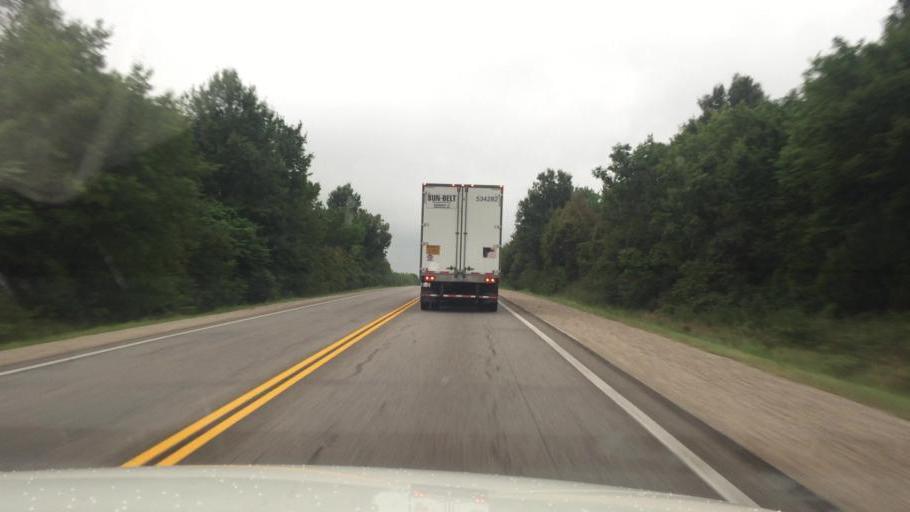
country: US
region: Kansas
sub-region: Montgomery County
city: Coffeyville
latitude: 37.1503
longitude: -95.5769
